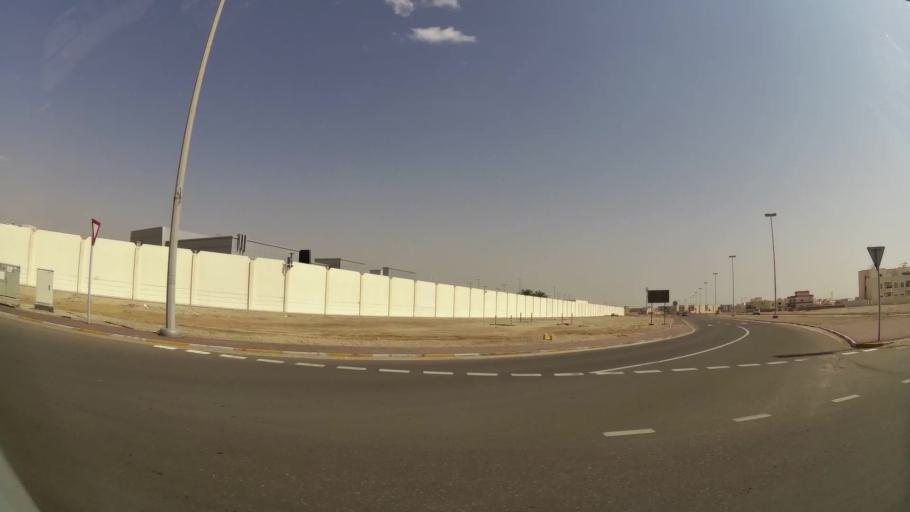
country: AE
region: Abu Dhabi
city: Abu Dhabi
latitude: 24.3156
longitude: 54.5526
